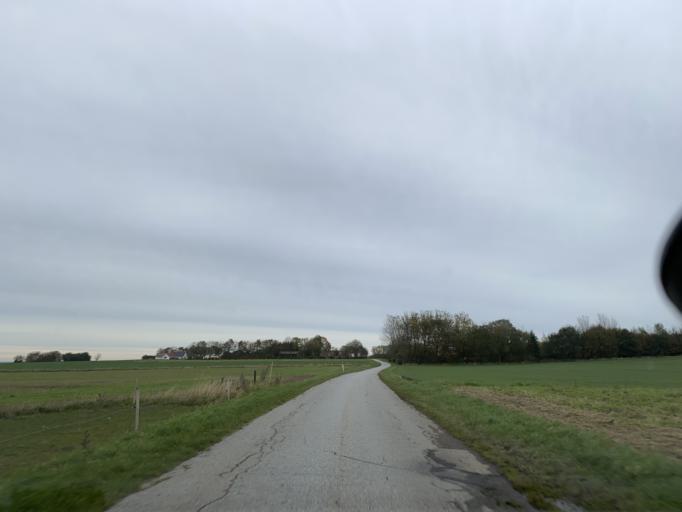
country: DK
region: Central Jutland
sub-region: Skanderborg Kommune
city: Ry
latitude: 56.1857
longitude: 9.7757
